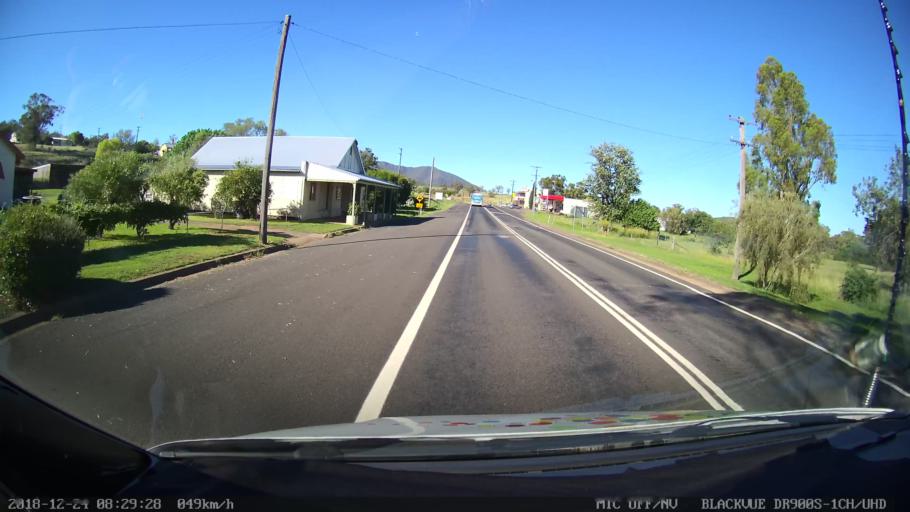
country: AU
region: New South Wales
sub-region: Tamworth Municipality
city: Phillip
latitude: -31.2632
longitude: 150.7337
